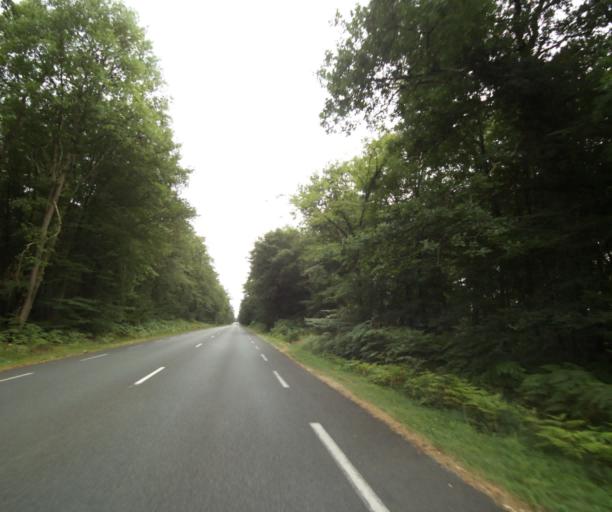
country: FR
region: Ile-de-France
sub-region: Departement de Seine-et-Marne
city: Bois-le-Roi
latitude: 48.4658
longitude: 2.6813
